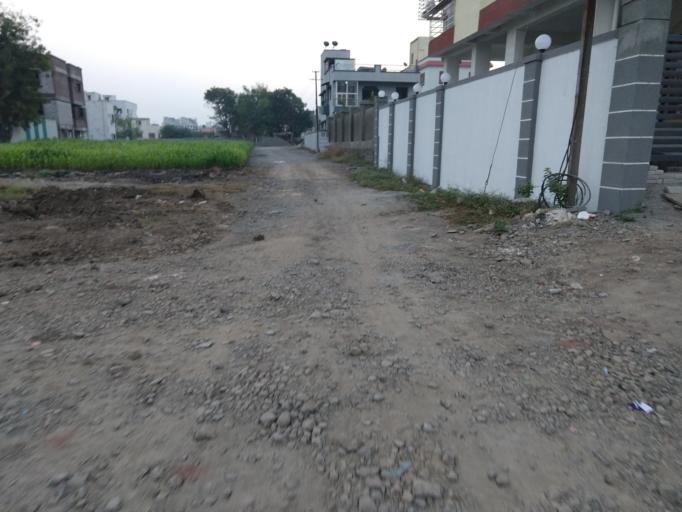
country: IN
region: Maharashtra
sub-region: Pune Division
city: Pune
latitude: 18.4386
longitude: 73.9129
